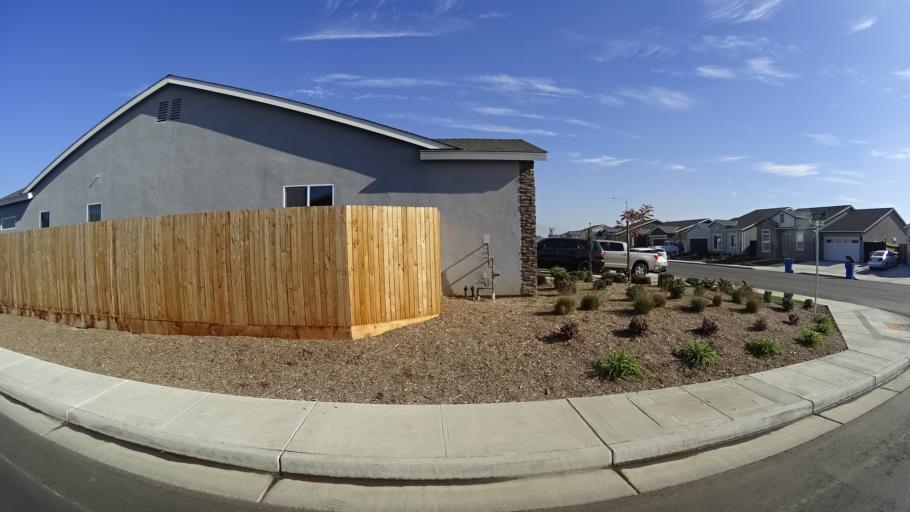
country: US
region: California
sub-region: Kern County
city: Greenfield
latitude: 35.2903
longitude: -119.0676
